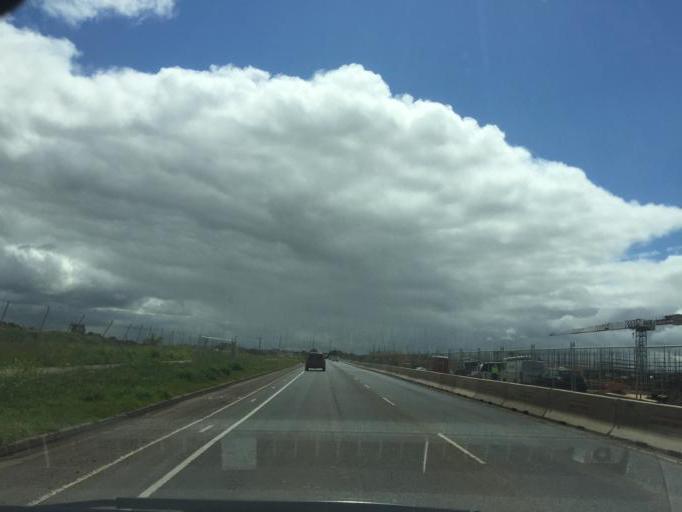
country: AU
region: Victoria
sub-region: Brimbank
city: Albion
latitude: -37.7706
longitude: 144.8487
